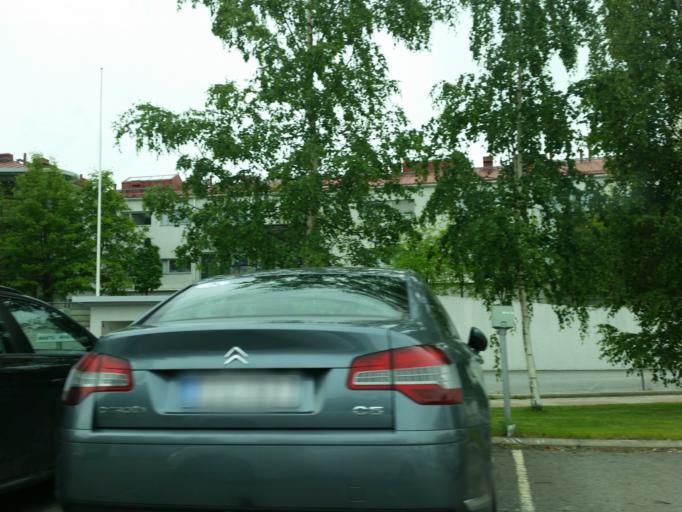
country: FI
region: Northern Savo
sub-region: Kuopio
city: Kuopio
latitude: 62.8938
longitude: 27.6940
